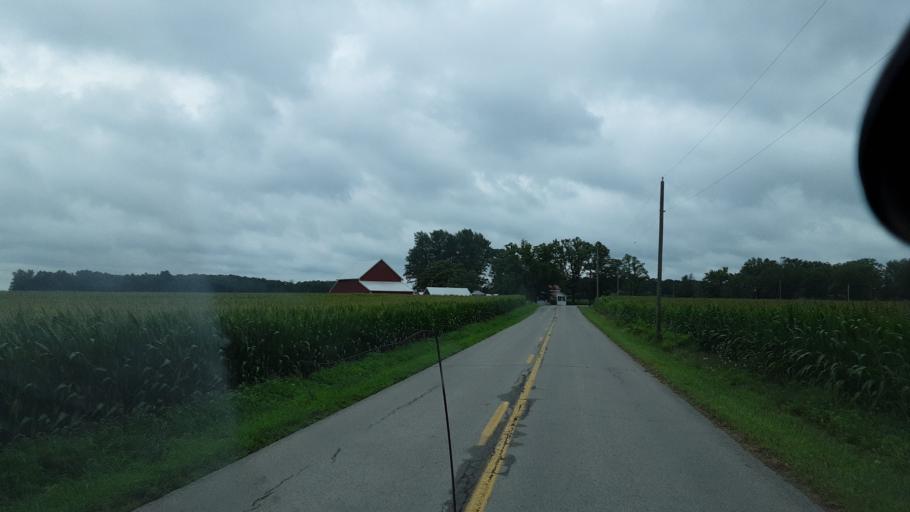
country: US
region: Indiana
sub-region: Wells County
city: Ossian
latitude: 40.9335
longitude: -85.0896
